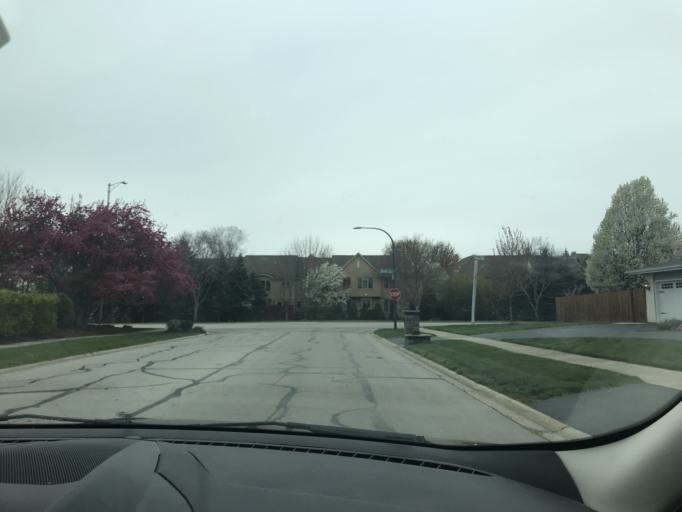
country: US
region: Illinois
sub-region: DuPage County
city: Naperville
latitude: 41.7355
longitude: -88.1166
